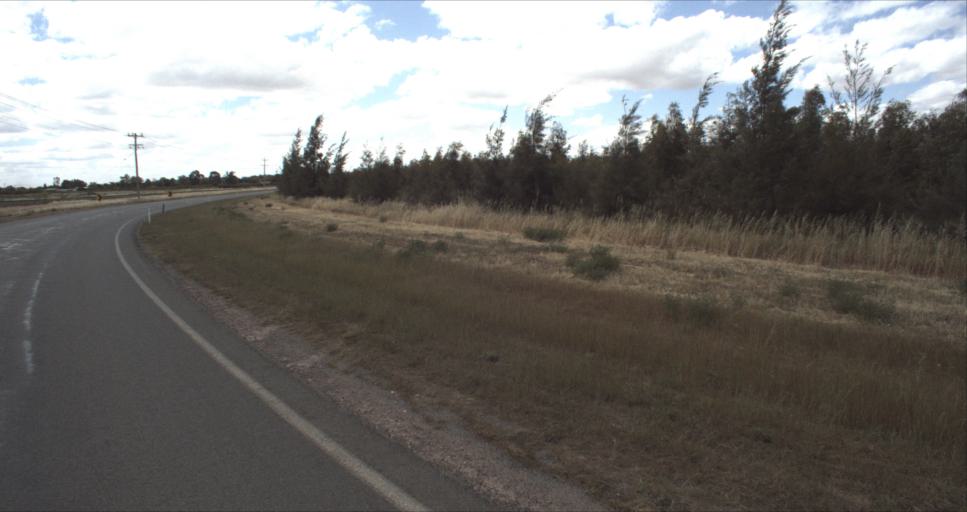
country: AU
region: New South Wales
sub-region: Leeton
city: Leeton
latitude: -34.5767
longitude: 146.3957
